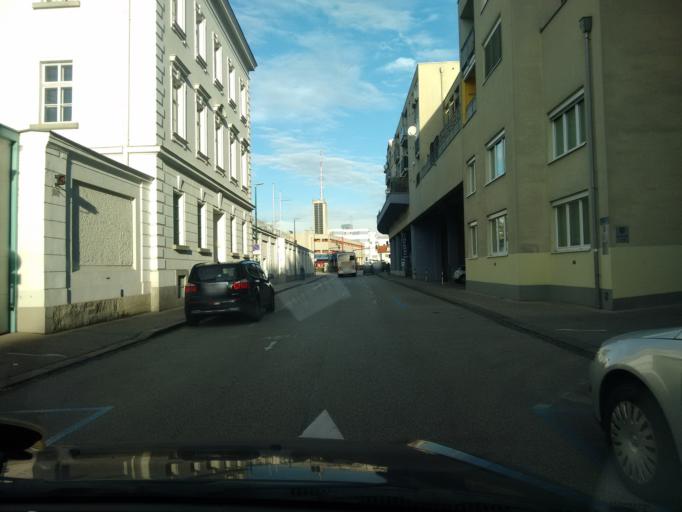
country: AT
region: Upper Austria
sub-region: Wels-Land
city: Thalheim bei Wels
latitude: 48.1573
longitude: 14.0200
